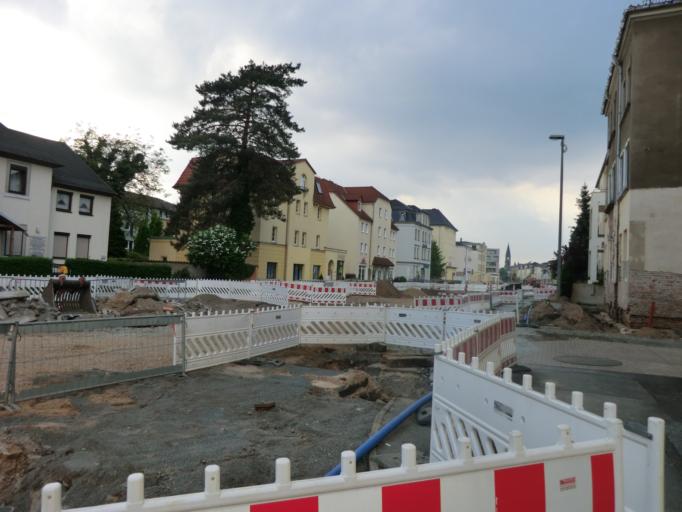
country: DE
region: Saxony
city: Albertstadt
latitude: 51.0382
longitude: 13.8087
